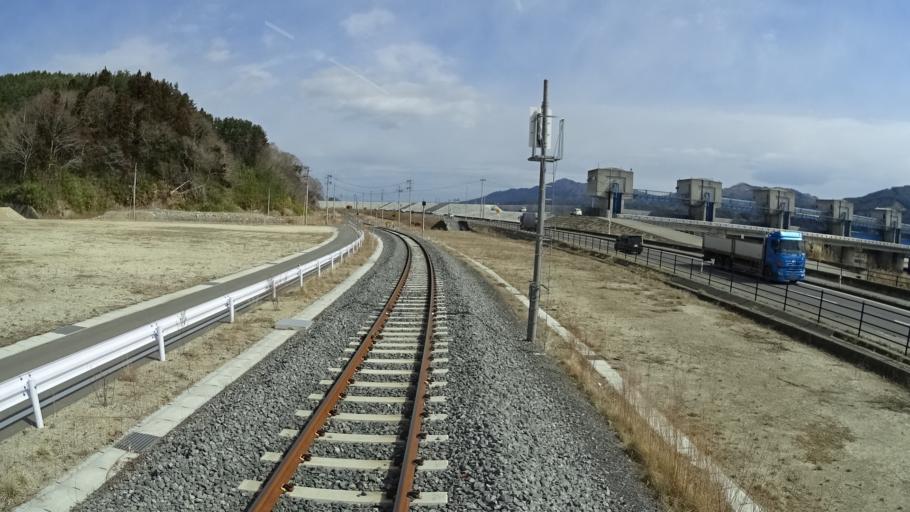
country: JP
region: Iwate
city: Miyako
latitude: 39.5850
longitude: 141.9435
